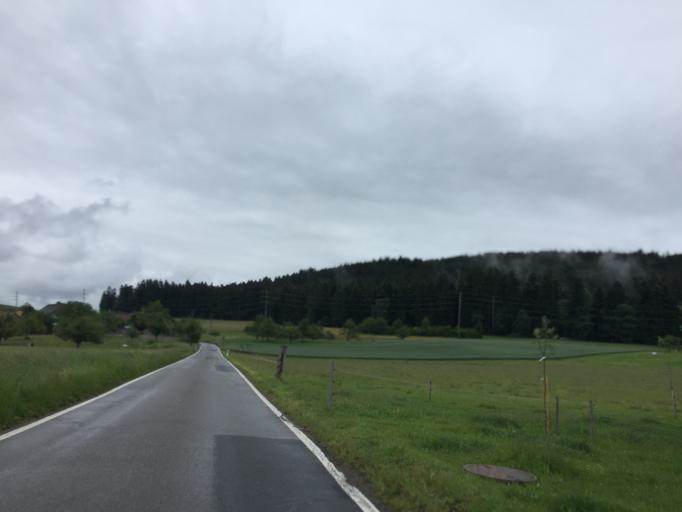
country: CH
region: Bern
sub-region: Bern-Mittelland District
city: Biglen
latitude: 46.9068
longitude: 7.6136
